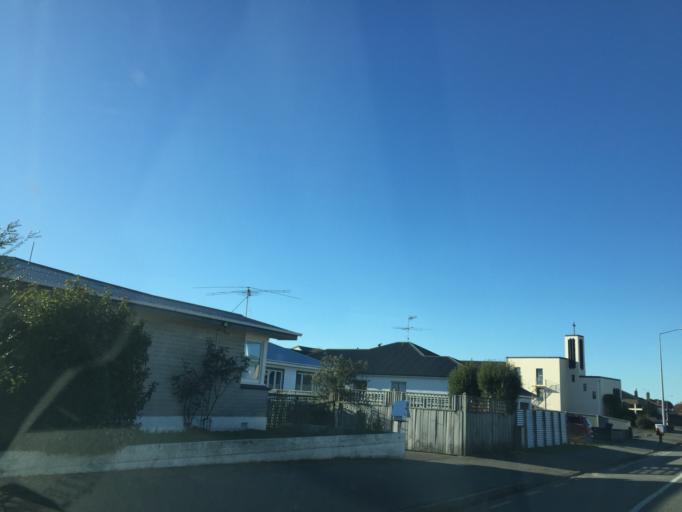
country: NZ
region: Southland
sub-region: Invercargill City
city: Invercargill
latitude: -46.4064
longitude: 168.3741
